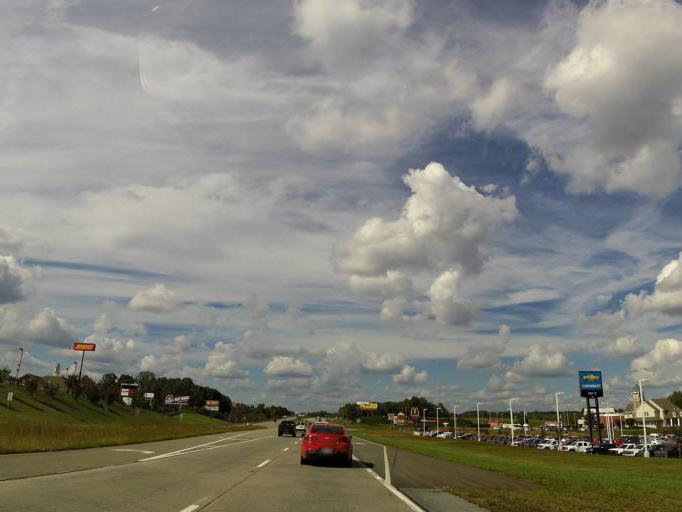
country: US
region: Georgia
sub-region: Pickens County
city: Jasper
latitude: 34.4604
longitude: -84.4558
